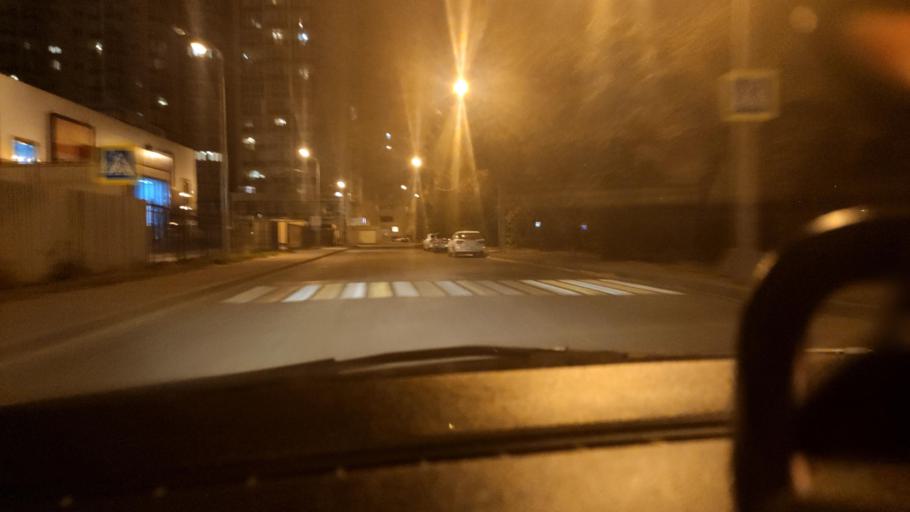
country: RU
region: Voronezj
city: Voronezh
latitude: 51.6425
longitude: 39.1428
